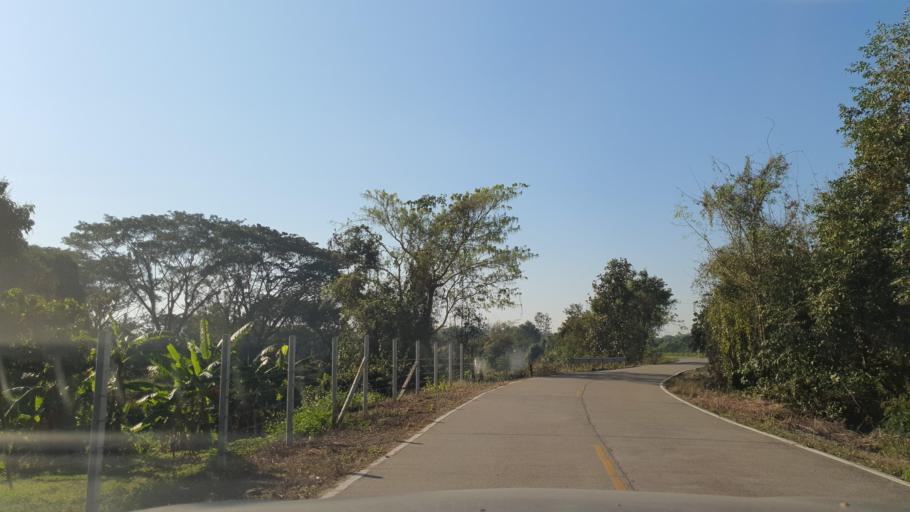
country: TH
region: Chiang Mai
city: Saraphi
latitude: 18.6851
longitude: 99.0804
